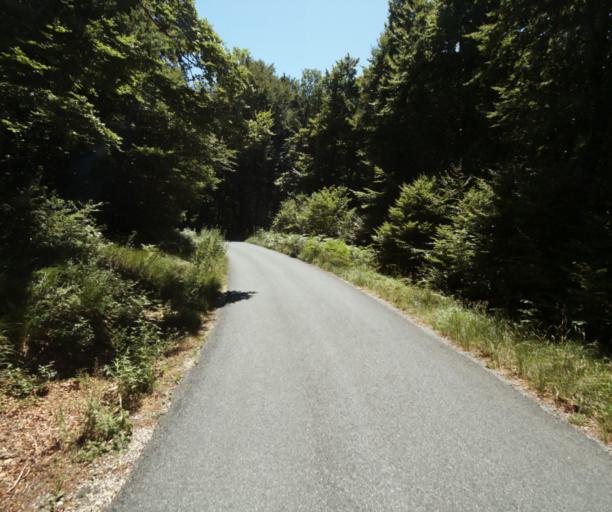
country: FR
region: Midi-Pyrenees
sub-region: Departement du Tarn
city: Dourgne
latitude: 43.4210
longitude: 2.1844
